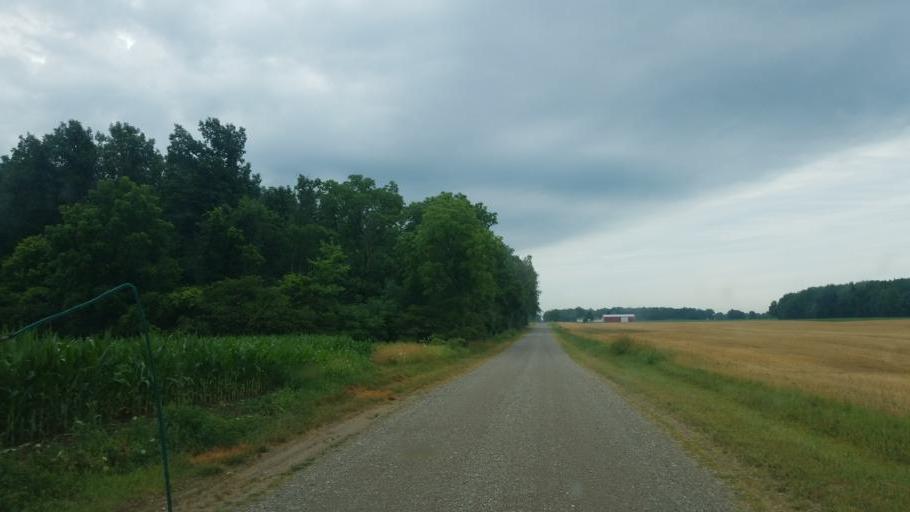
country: US
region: Indiana
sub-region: Steuben County
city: Hamilton
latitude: 41.4920
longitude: -84.9109
